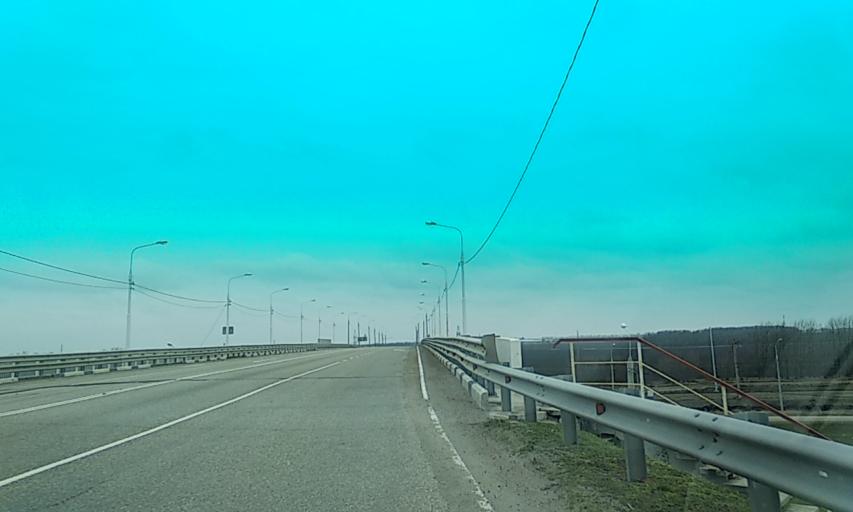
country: RU
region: Krasnodarskiy
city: Vyselki
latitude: 45.6158
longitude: 39.6964
